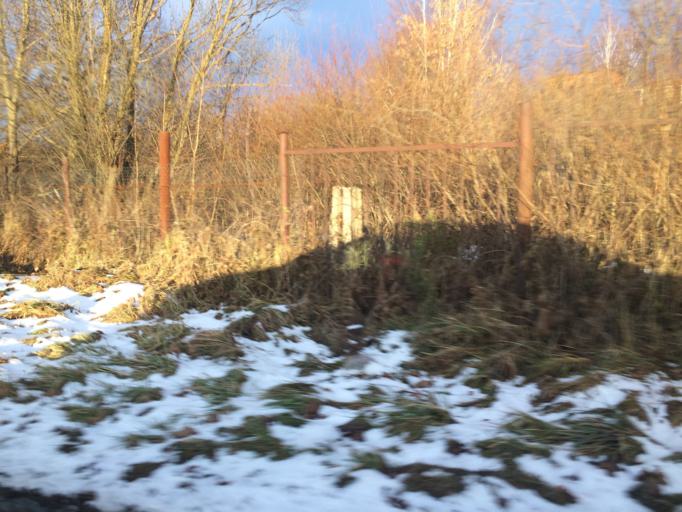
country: RU
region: Tula
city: Cherepet'
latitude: 54.1131
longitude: 36.3316
